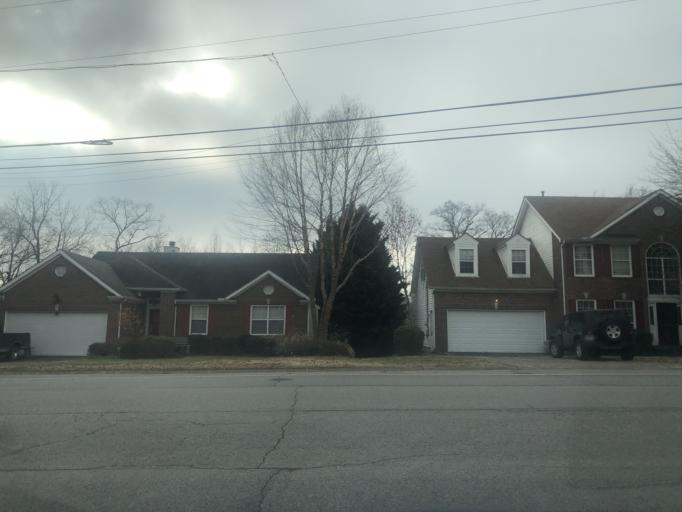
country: US
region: Tennessee
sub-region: Rutherford County
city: La Vergne
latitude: 36.0714
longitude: -86.6531
